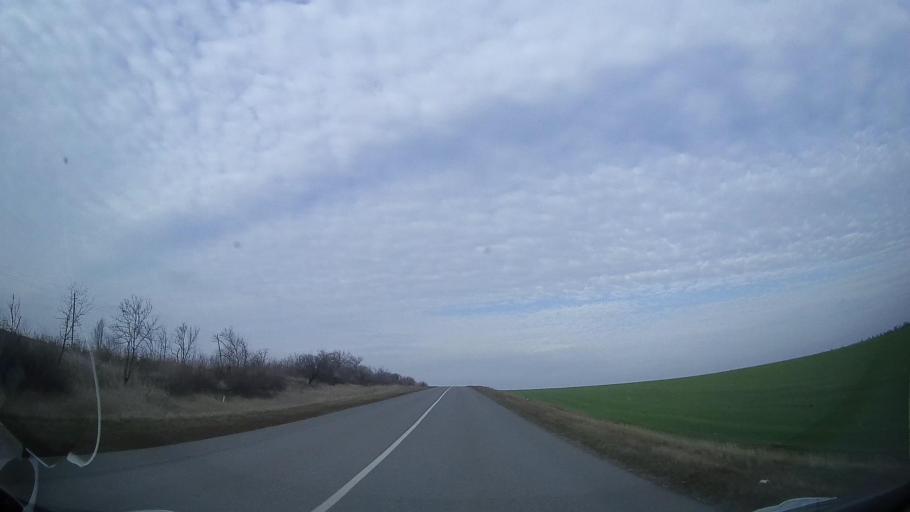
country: RU
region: Rostov
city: Zernograd
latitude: 46.9053
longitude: 40.3389
